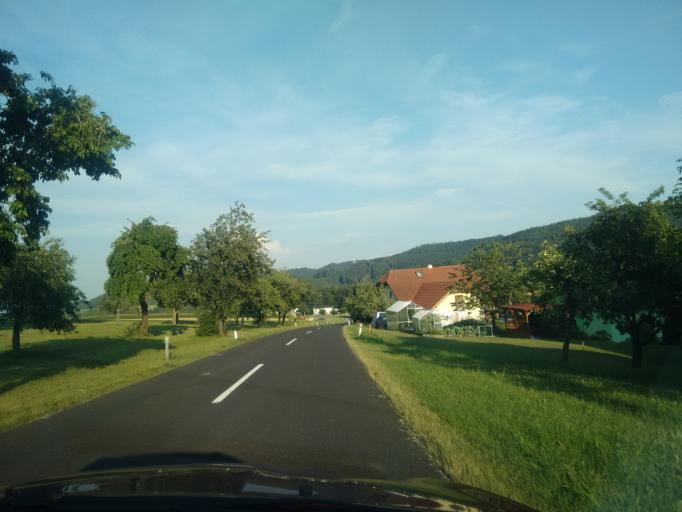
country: AT
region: Upper Austria
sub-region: Politischer Bezirk Vocklabruck
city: Wolfsegg am Hausruck
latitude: 48.1489
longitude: 13.6232
